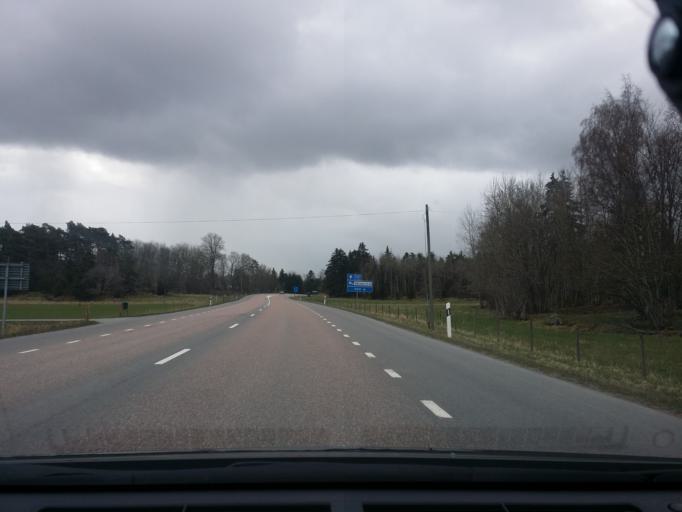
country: SE
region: Uppsala
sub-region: Enkopings Kommun
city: Irsta
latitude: 59.7357
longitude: 16.9551
